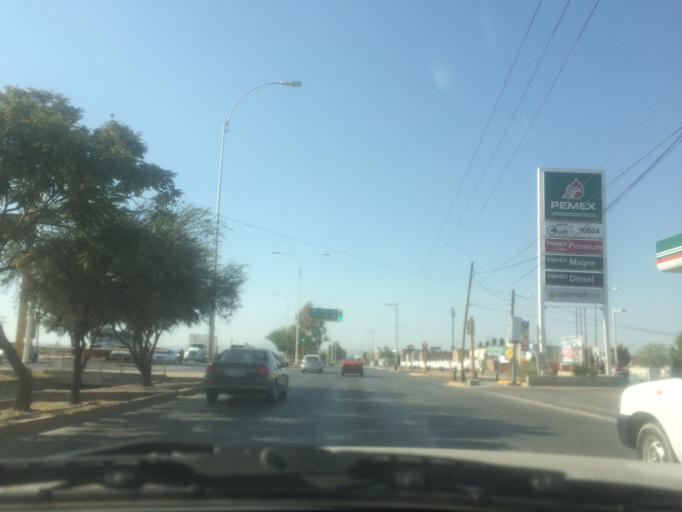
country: MX
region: Guanajuato
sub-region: Leon
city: San Jose de Duran (Los Troncoso)
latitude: 21.0762
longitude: -101.6516
